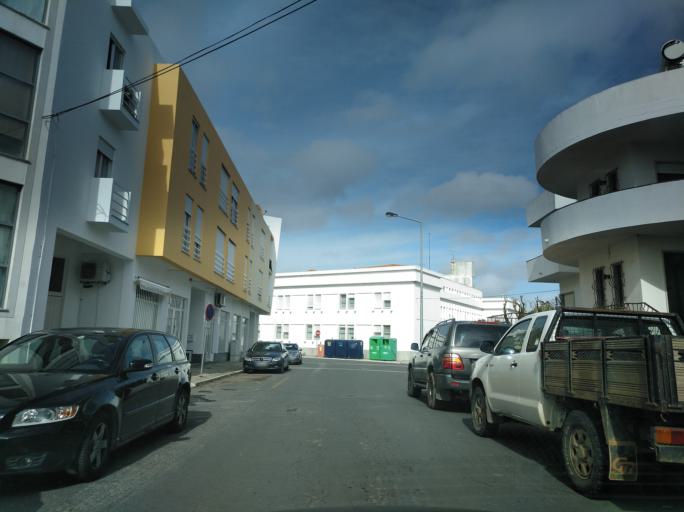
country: PT
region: Setubal
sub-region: Grandola
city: Grandola
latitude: 38.1780
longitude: -8.5618
